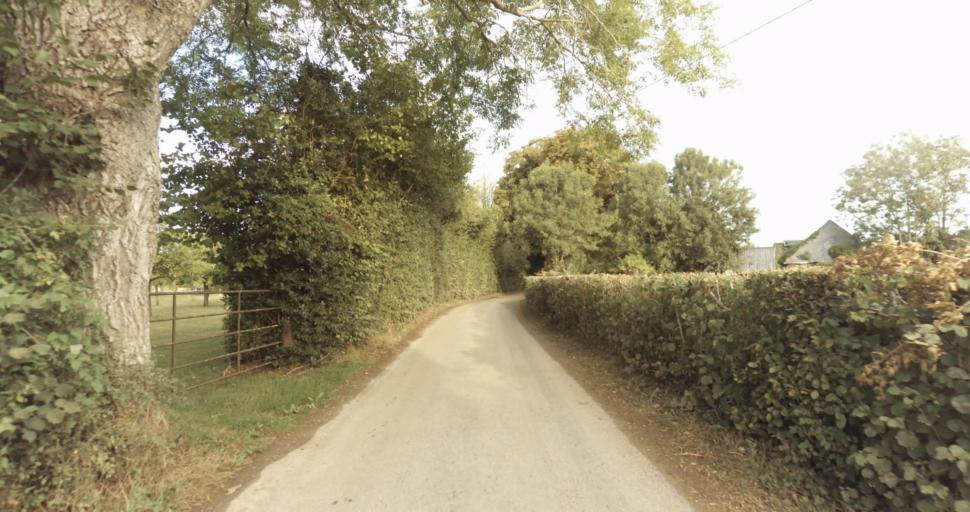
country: FR
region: Lower Normandy
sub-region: Departement de l'Orne
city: Vimoutiers
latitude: 48.8937
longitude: 0.2308
